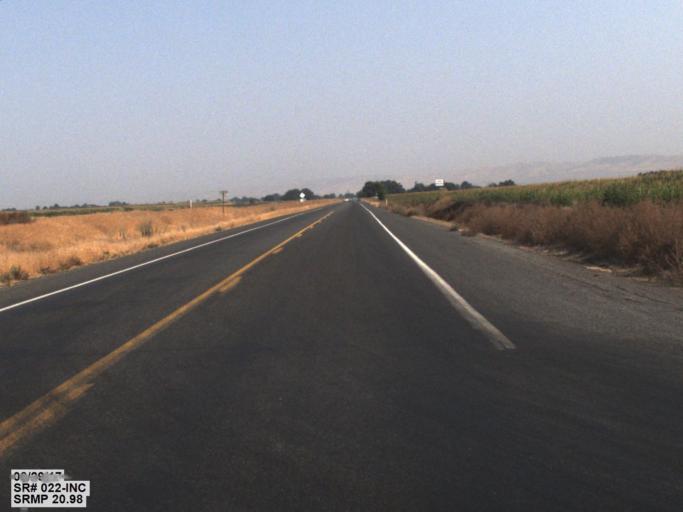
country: US
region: Washington
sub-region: Yakima County
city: Mabton
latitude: 46.2219
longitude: -120.0417
